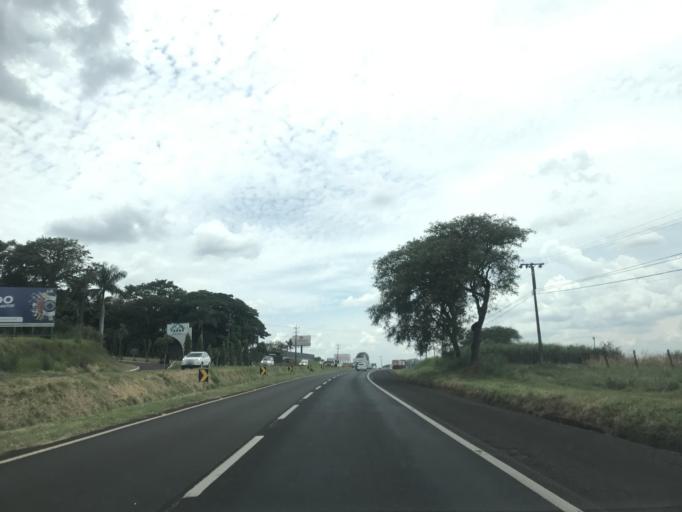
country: BR
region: Parana
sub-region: Paicandu
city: Paicandu
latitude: -23.3905
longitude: -52.0143
